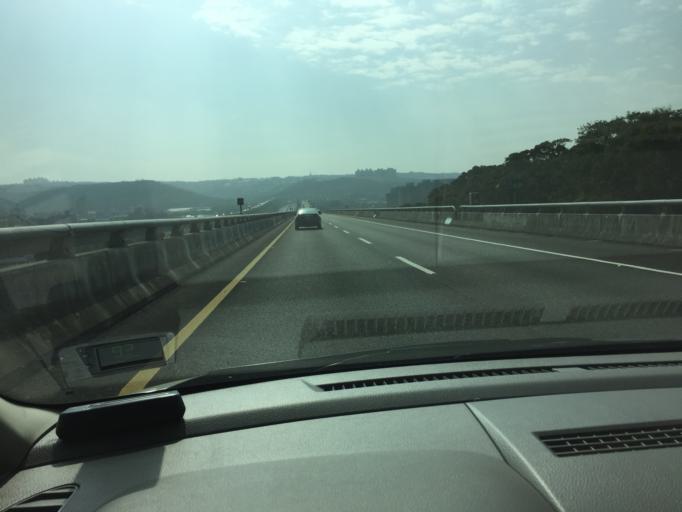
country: TW
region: Taiwan
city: Daxi
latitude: 24.9192
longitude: 121.1678
